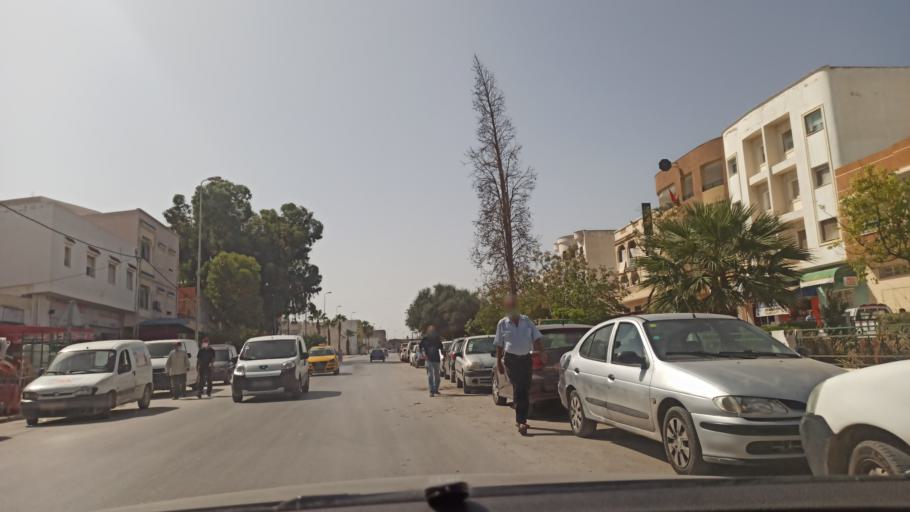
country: TN
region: Manouba
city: Manouba
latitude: 36.7661
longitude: 10.1110
